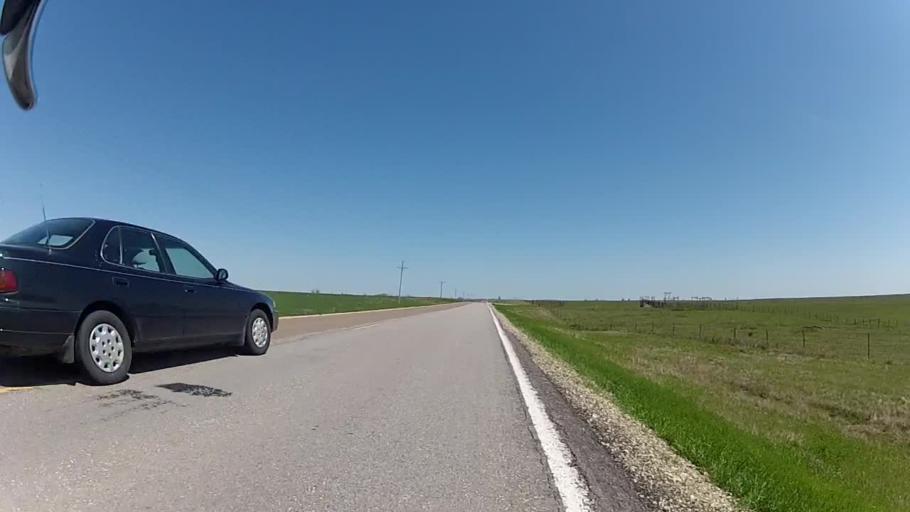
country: US
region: Kansas
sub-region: Morris County
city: Council Grove
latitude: 38.8853
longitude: -96.5202
